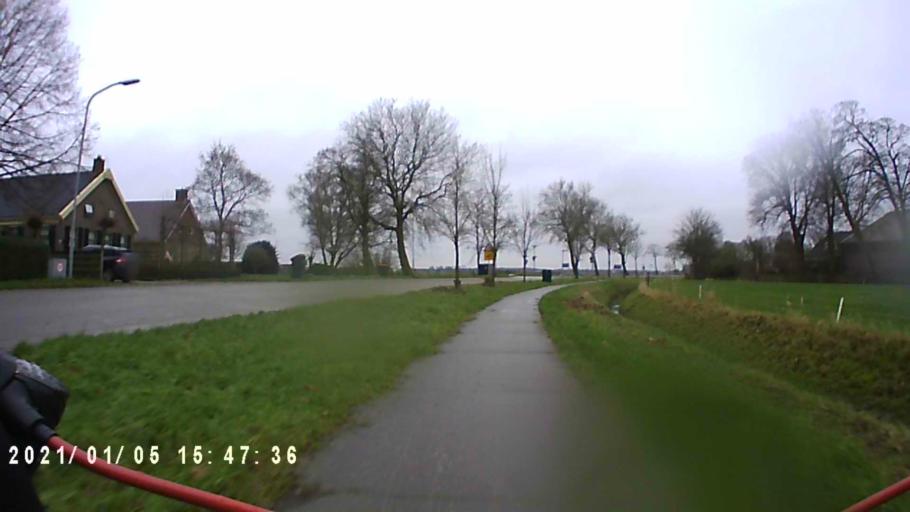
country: NL
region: Groningen
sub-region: Gemeente  Oldambt
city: Winschoten
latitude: 53.2023
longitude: 7.1149
